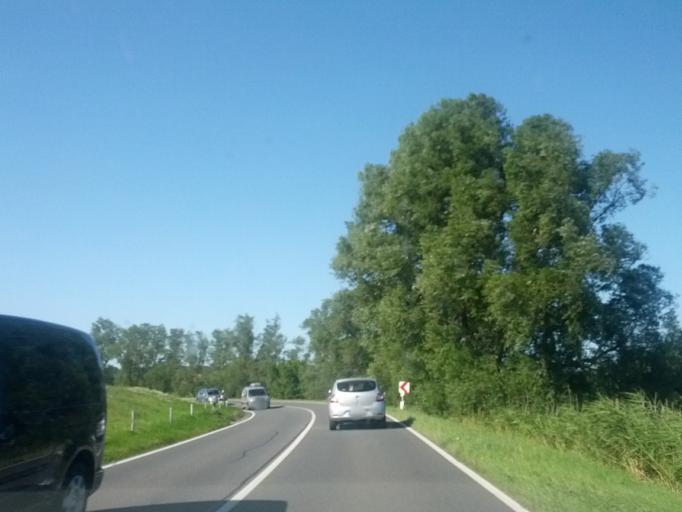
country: DE
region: Mecklenburg-Vorpommern
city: Ostseebad Gohren
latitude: 54.3258
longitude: 13.7081
